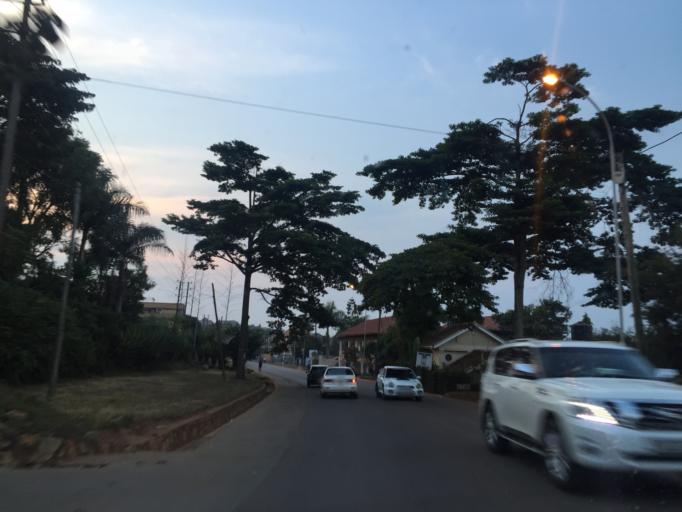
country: UG
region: Central Region
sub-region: Kampala District
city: Kampala
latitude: 0.2459
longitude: 32.6280
